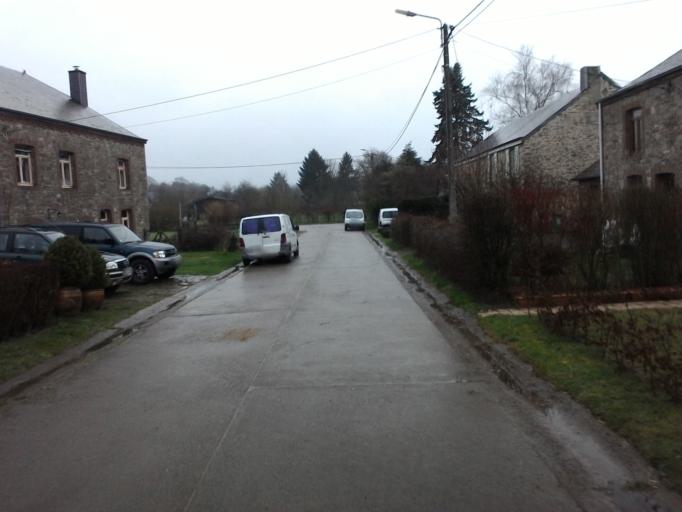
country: FR
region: Champagne-Ardenne
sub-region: Departement des Ardennes
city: Fromelennes
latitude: 50.0271
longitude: 4.8522
